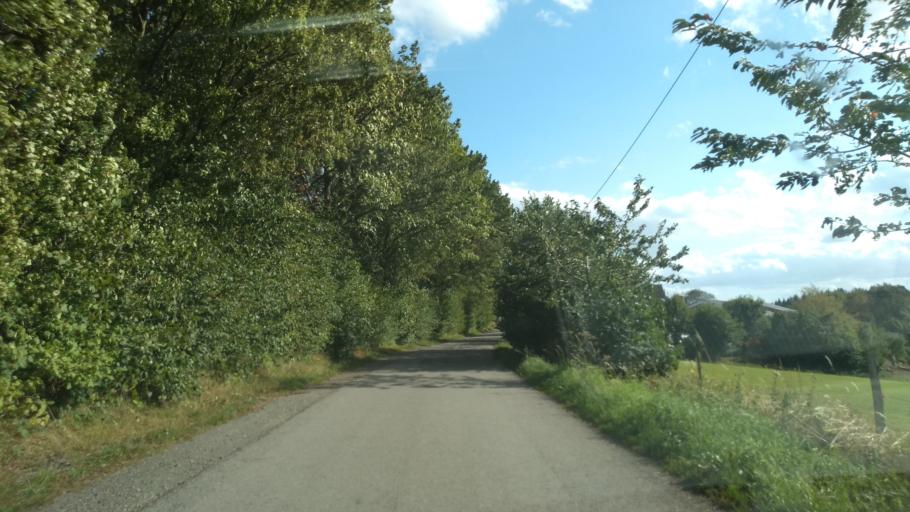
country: DE
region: North Rhine-Westphalia
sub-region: Regierungsbezirk Arnsberg
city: Schalksmuhle
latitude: 51.2189
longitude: 7.5485
